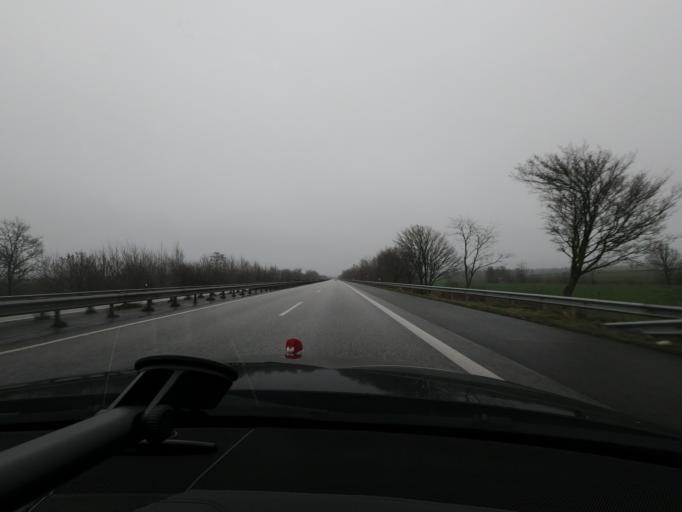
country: DE
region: Schleswig-Holstein
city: Bollingstedt
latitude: 54.6020
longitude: 9.4518
